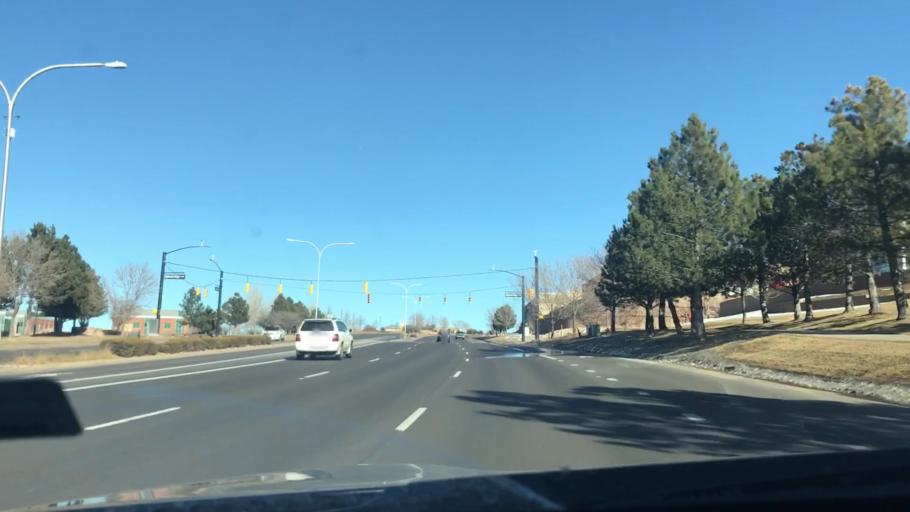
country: US
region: Colorado
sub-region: El Paso County
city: Air Force Academy
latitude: 38.9652
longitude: -104.7900
